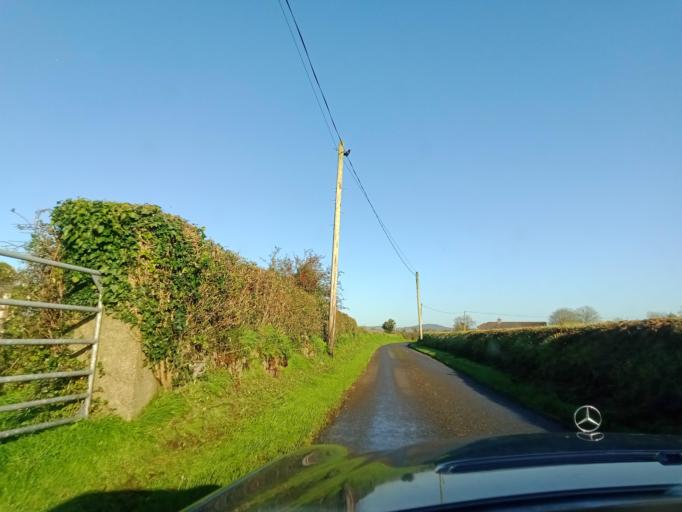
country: IE
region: Leinster
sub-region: Kilkenny
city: Mooncoin
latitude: 52.2886
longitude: -7.2109
